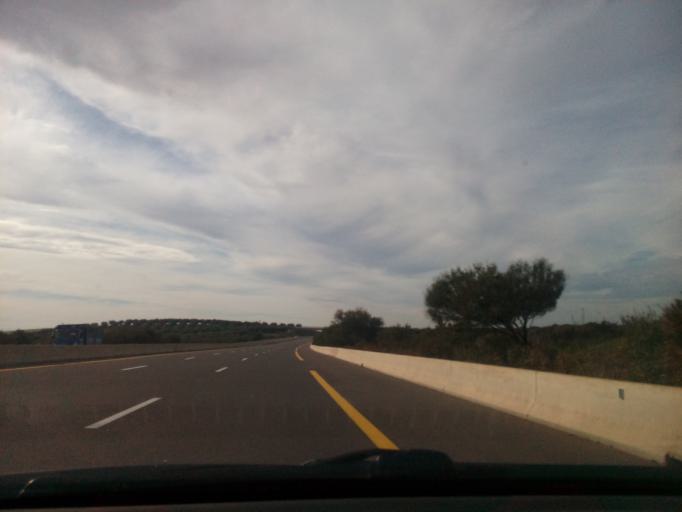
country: DZ
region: Sidi Bel Abbes
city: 'Ain el Berd
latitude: 35.3405
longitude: -0.5179
